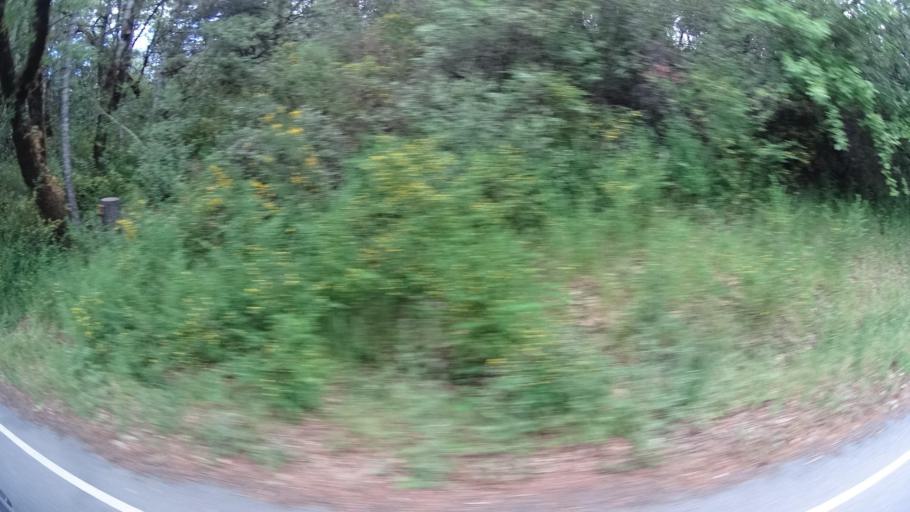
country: US
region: California
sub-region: Humboldt County
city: Redway
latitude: 40.1063
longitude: -123.7904
